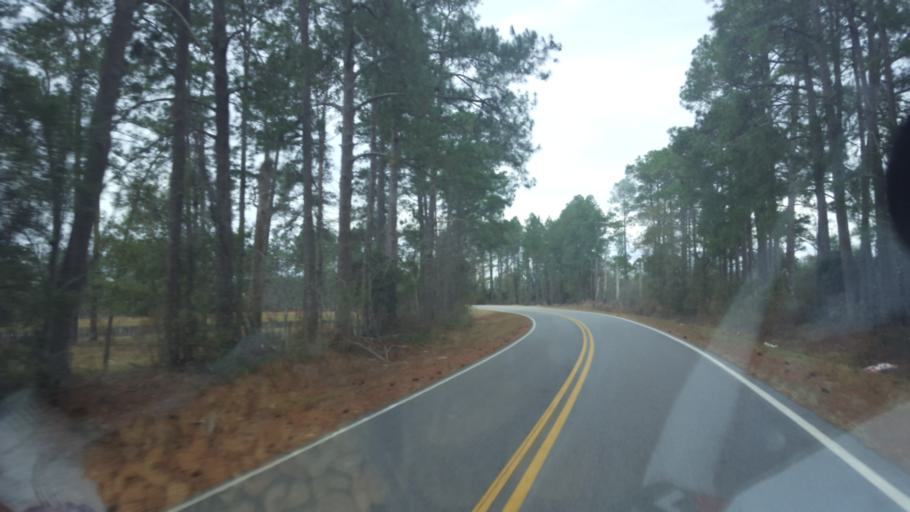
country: US
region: Georgia
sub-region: Wilcox County
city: Rochelle
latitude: 31.8109
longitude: -83.4613
